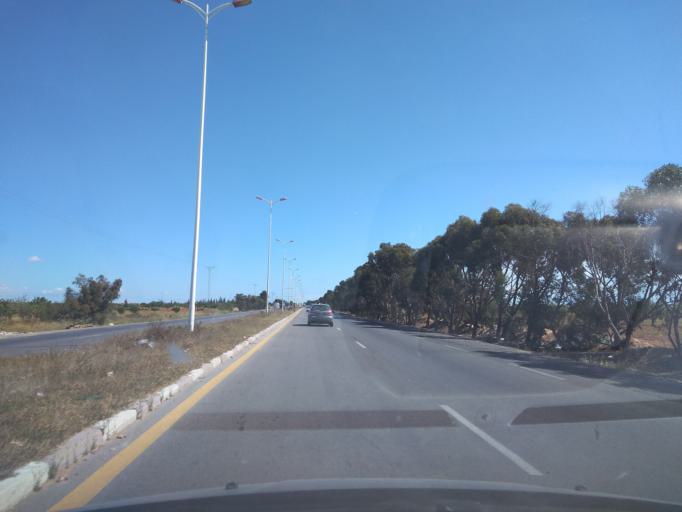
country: TN
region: Safaqis
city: Sfax
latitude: 34.8287
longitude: 10.7211
